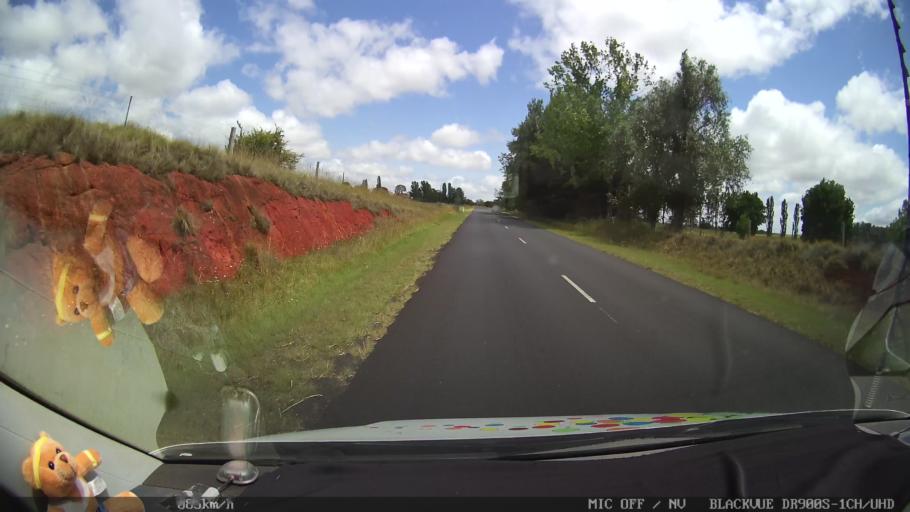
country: AU
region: New South Wales
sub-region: Glen Innes Severn
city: Glen Innes
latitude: -29.7073
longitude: 151.7211
